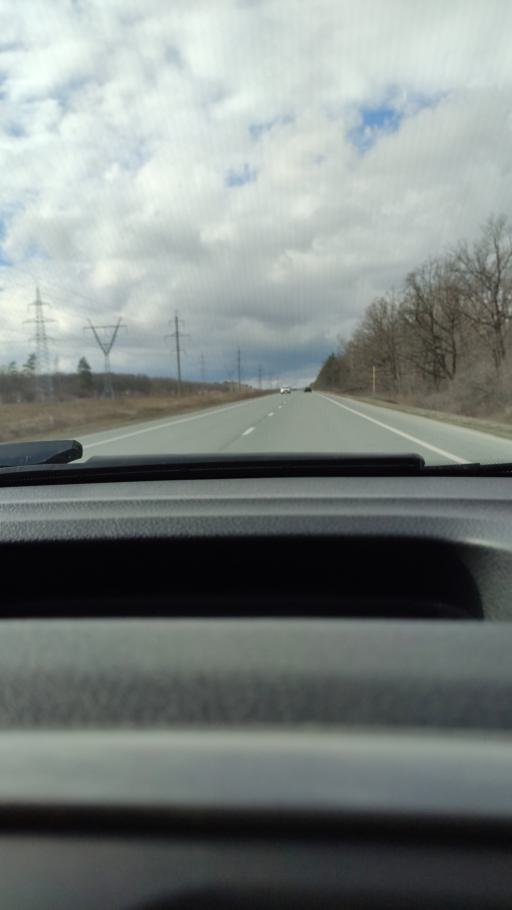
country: RU
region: Samara
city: Bogatyr'
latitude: 53.4998
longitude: 49.9536
